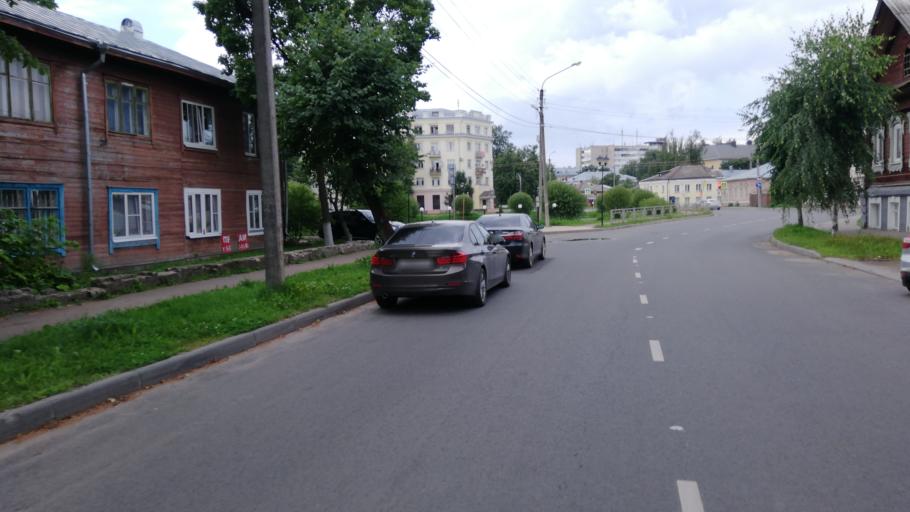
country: RU
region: Kostroma
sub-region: Kostromskoy Rayon
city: Kostroma
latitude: 57.7679
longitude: 40.9357
